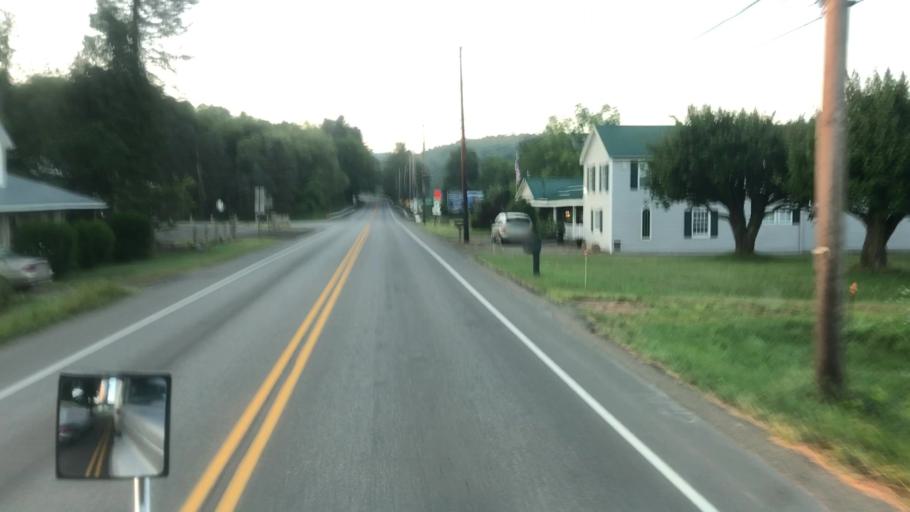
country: US
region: Pennsylvania
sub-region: Crawford County
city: Titusville
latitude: 41.6201
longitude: -79.6404
